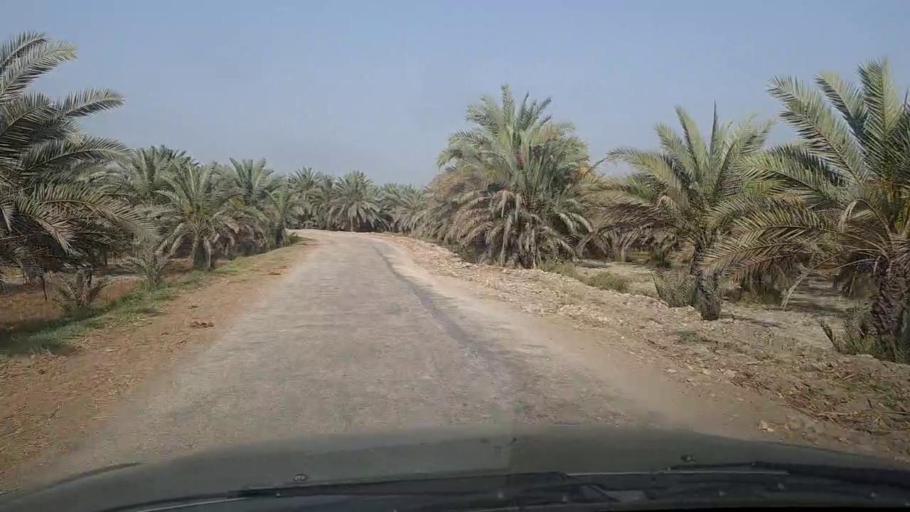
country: PK
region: Sindh
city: Pir jo Goth
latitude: 27.5549
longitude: 68.5379
